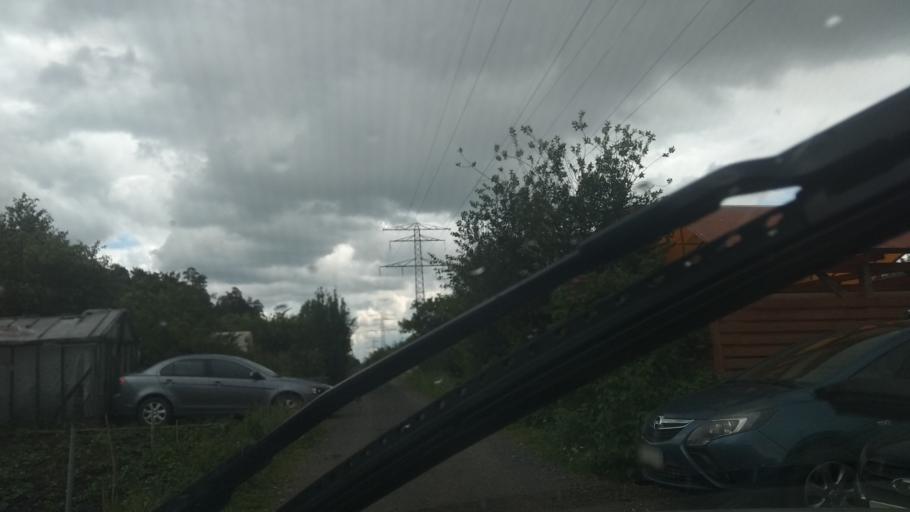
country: RU
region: Sverdlovsk
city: Verkhnyaya Pyshma
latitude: 56.9190
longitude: 60.5800
